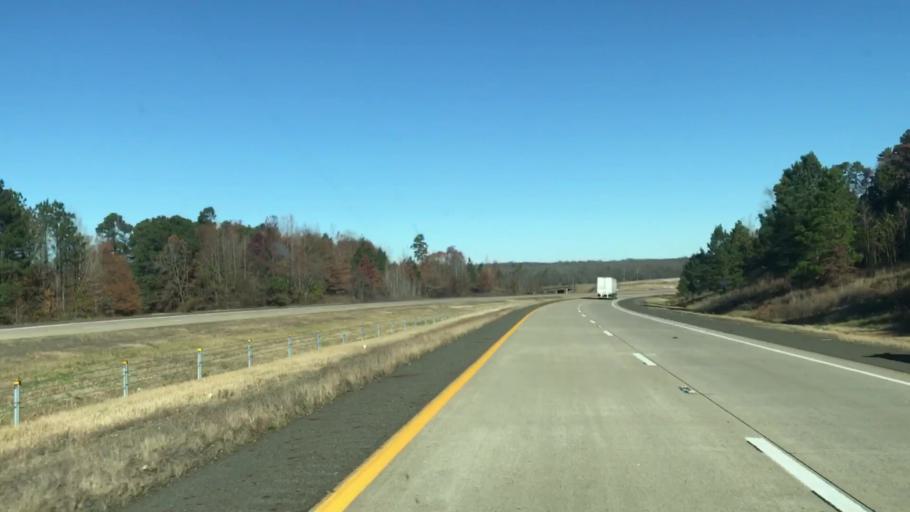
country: US
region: Texas
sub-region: Cass County
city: Queen City
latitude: 33.1323
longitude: -93.8942
